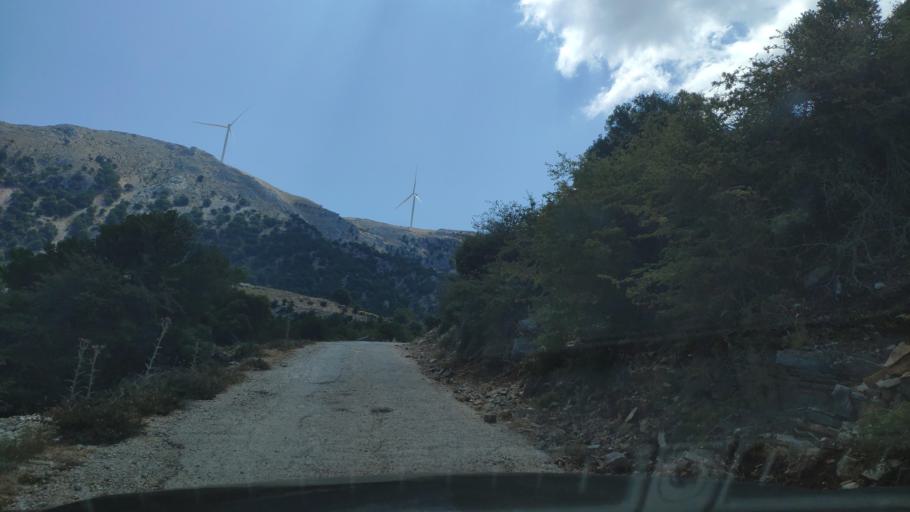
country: GR
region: West Greece
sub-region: Nomos Aitolias kai Akarnanias
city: Monastirakion
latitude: 38.7849
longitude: 20.9810
